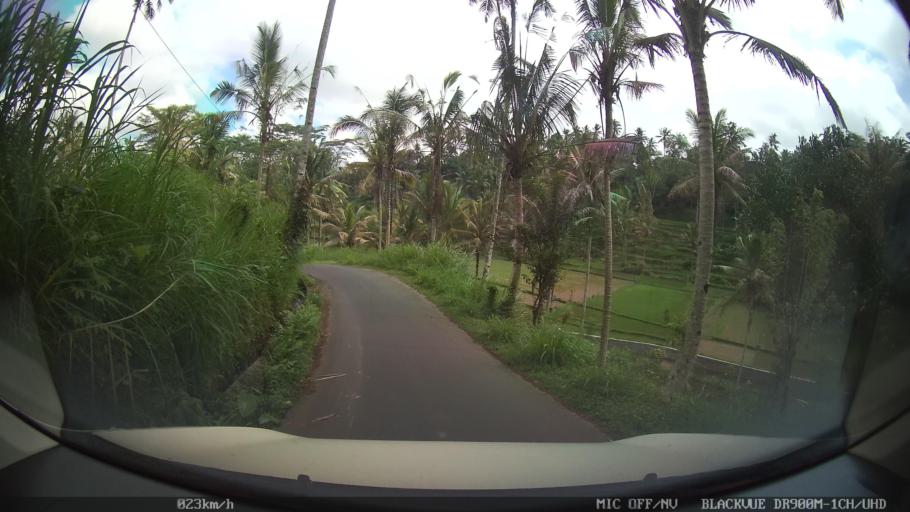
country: ID
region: Bali
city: Banjar Petak
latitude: -8.4478
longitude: 115.3273
